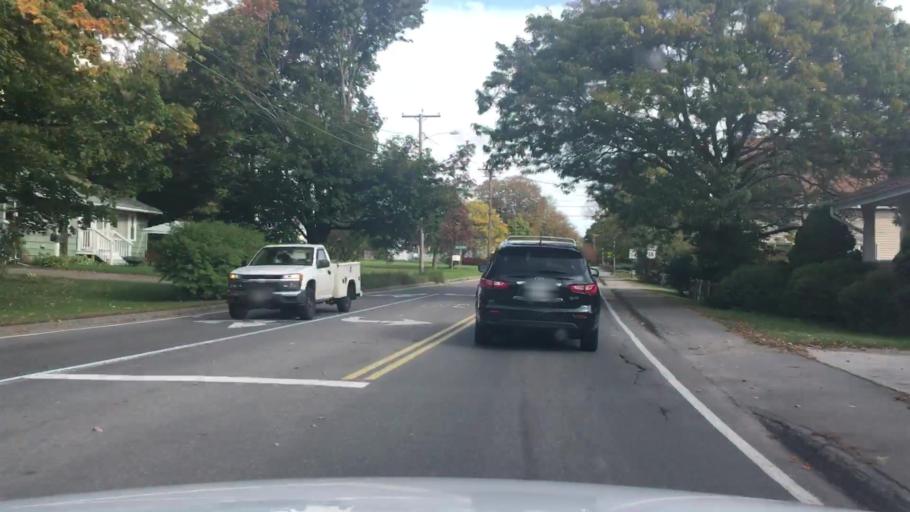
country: US
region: Maine
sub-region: Knox County
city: Rockland
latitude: 44.1111
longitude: -69.1156
